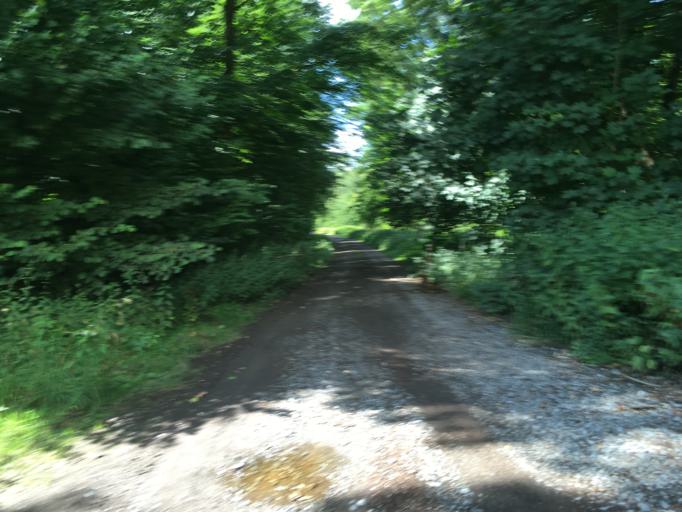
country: DE
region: Baden-Wuerttemberg
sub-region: Karlsruhe Region
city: Sinsheim
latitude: 49.1937
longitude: 8.8474
